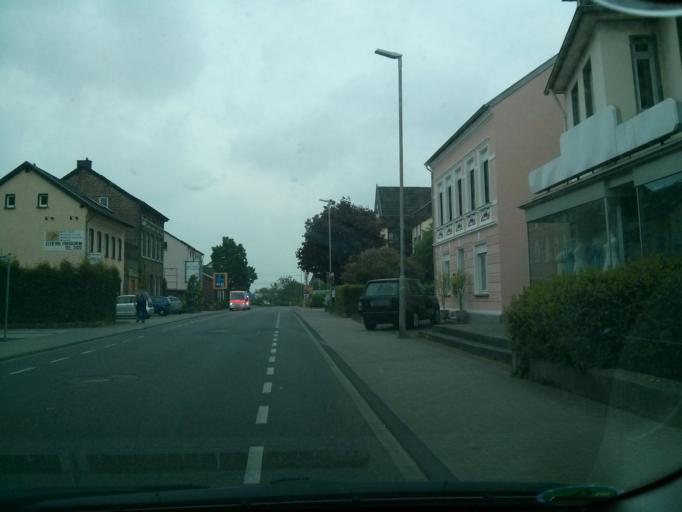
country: DE
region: North Rhine-Westphalia
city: Meckenheim
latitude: 50.6260
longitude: 7.0178
